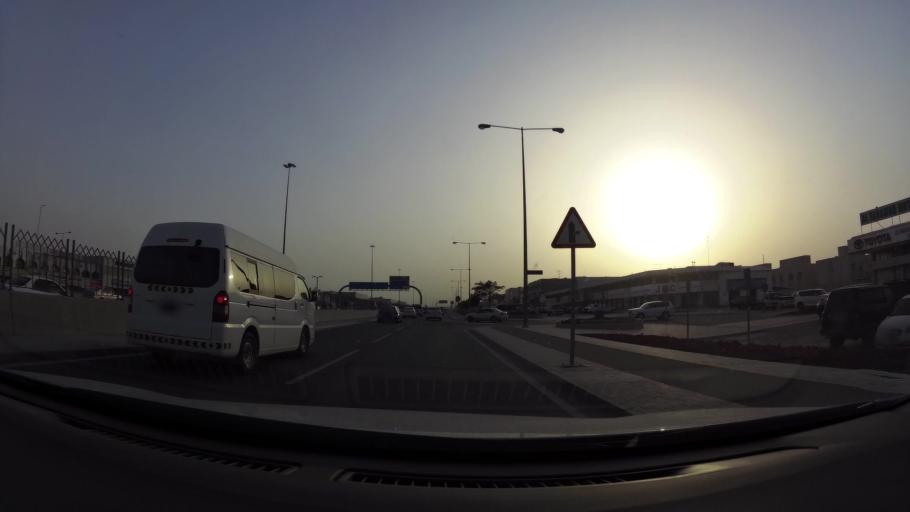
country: QA
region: Baladiyat ar Rayyan
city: Ar Rayyan
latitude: 25.2374
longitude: 51.4512
